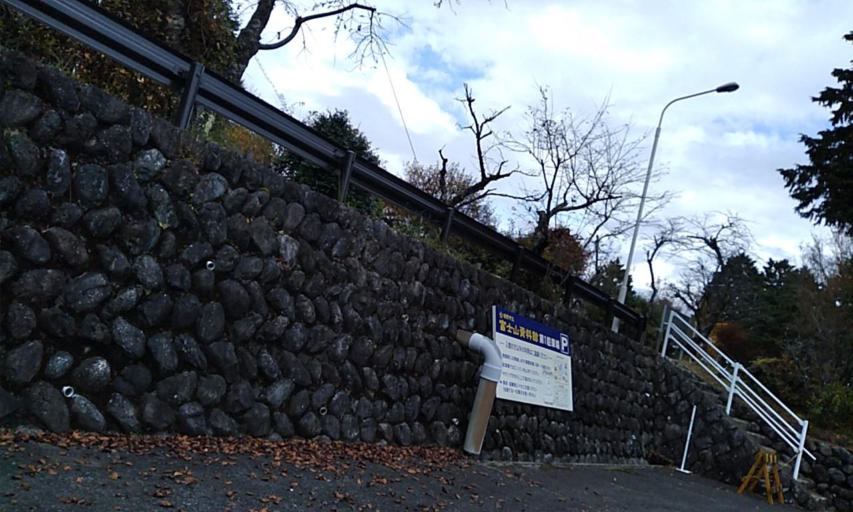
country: JP
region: Shizuoka
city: Gotemba
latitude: 35.2645
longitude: 138.8073
